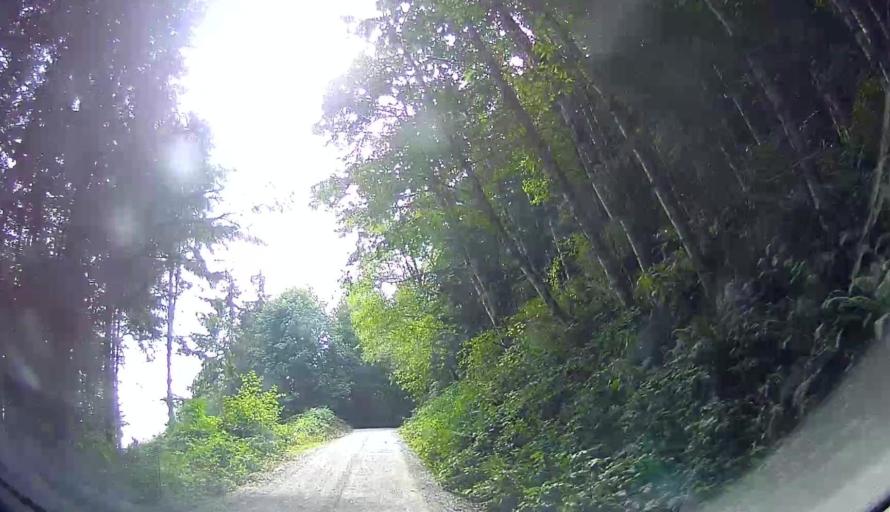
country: US
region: Washington
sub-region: Whatcom County
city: Sudden Valley
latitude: 48.6132
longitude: -122.3910
